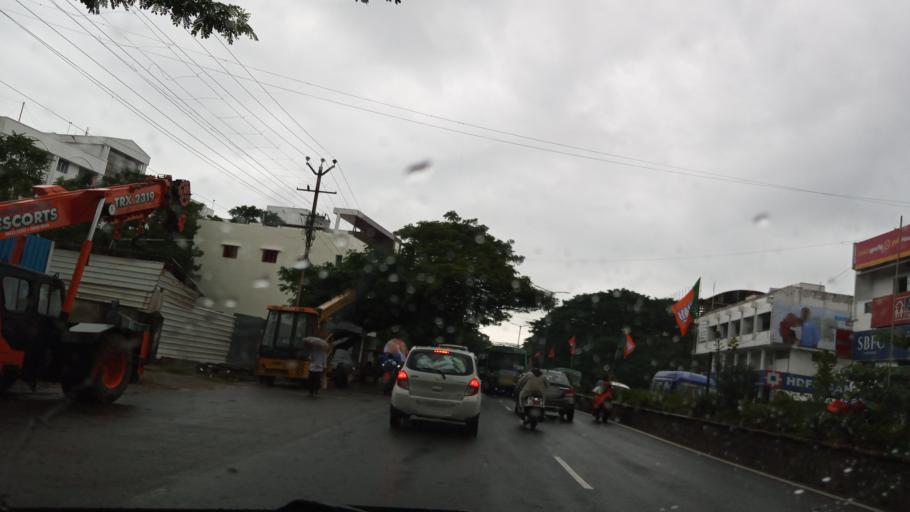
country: IN
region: Pondicherry
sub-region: Puducherry
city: Puducherry
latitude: 11.9337
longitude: 79.8075
